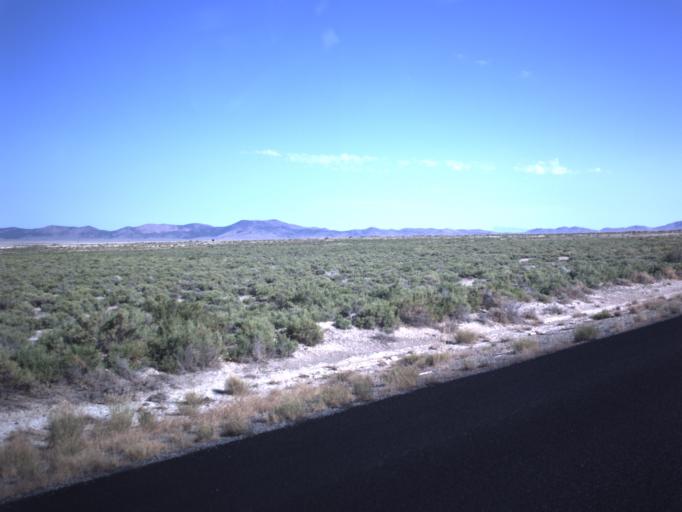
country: US
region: Utah
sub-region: Beaver County
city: Milford
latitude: 38.5254
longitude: -112.9912
